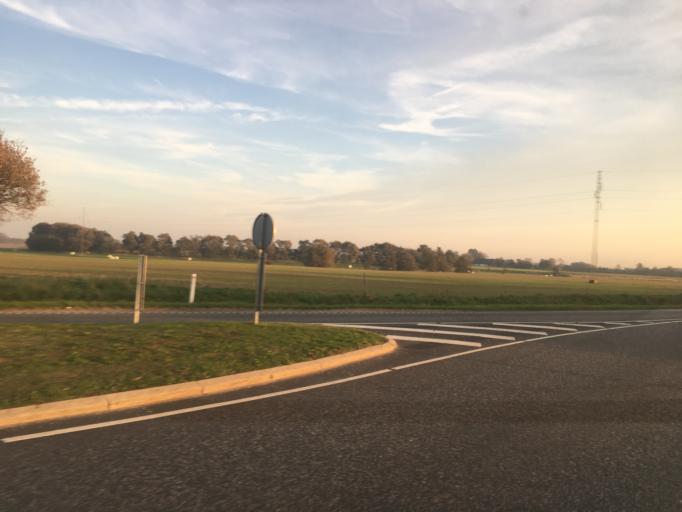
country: DK
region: South Denmark
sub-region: Tonder Kommune
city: Toftlund
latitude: 55.0514
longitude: 9.0944
